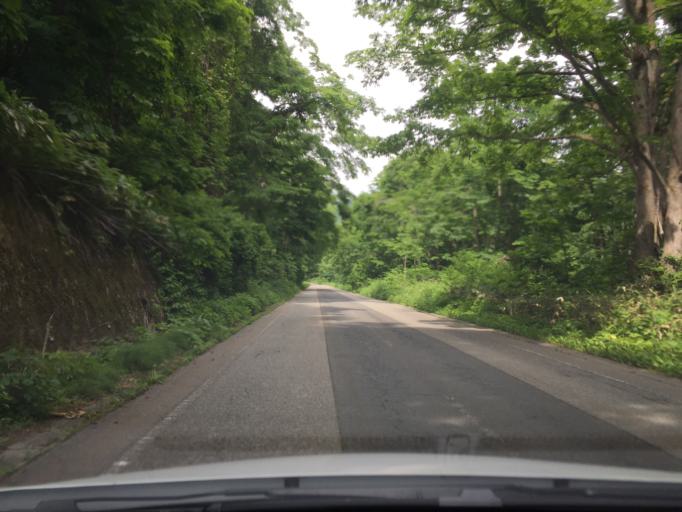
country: JP
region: Fukushima
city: Inawashiro
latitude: 37.6439
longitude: 140.0330
